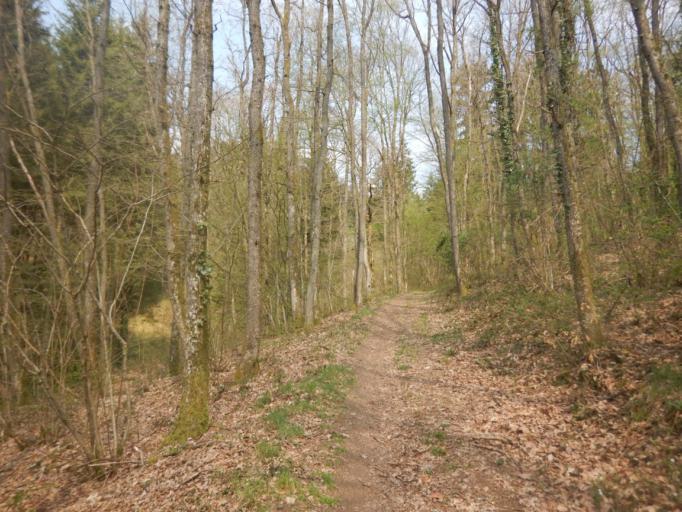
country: LU
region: Diekirch
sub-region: Canton de Wiltz
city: Esch-sur-Sure
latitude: 49.9148
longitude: 5.9172
